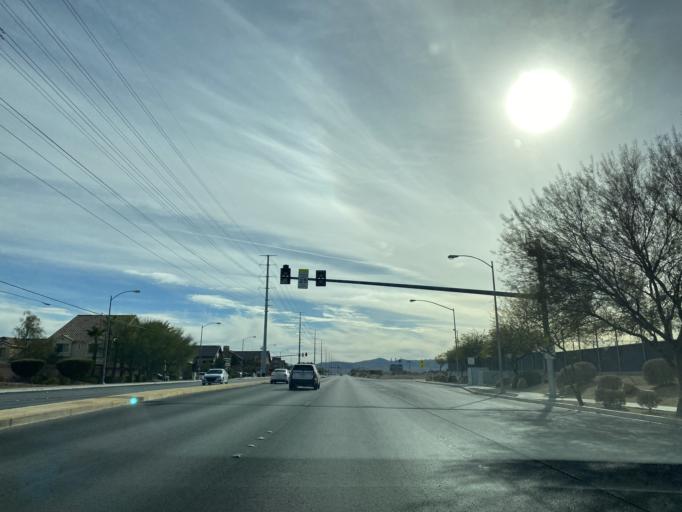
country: US
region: Nevada
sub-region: Clark County
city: Enterprise
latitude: 36.0389
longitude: -115.2431
